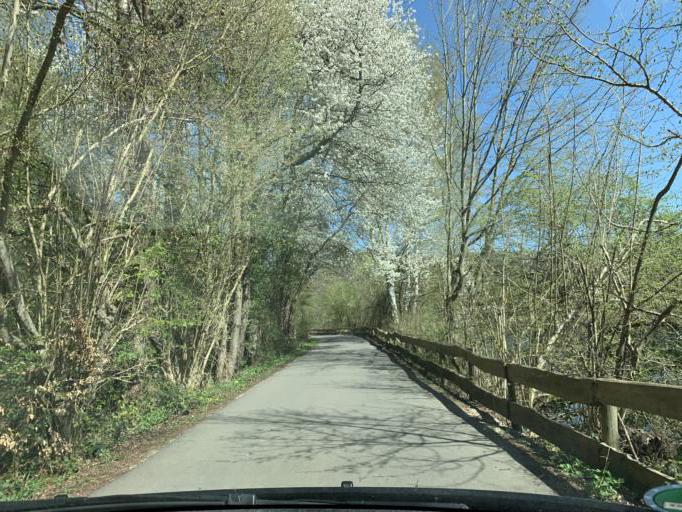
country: DE
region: North Rhine-Westphalia
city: Heimbach
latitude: 50.6309
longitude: 6.4515
